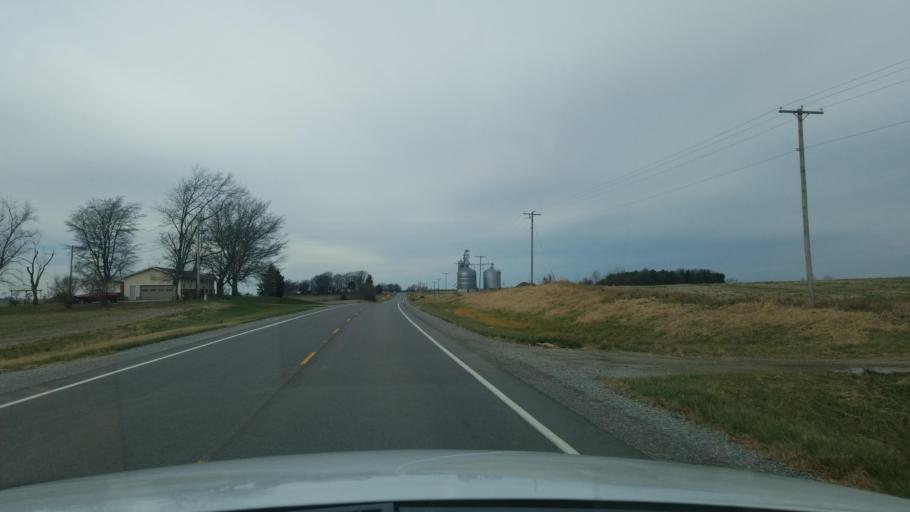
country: US
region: Illinois
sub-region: White County
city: Carmi
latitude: 37.9077
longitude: -88.1449
